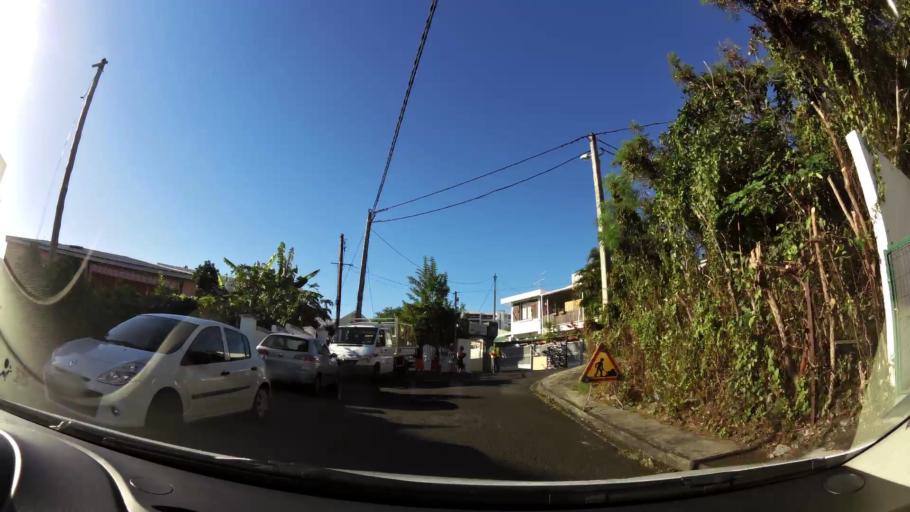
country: RE
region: Reunion
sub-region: Reunion
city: Saint-Denis
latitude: -20.8918
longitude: 55.4480
